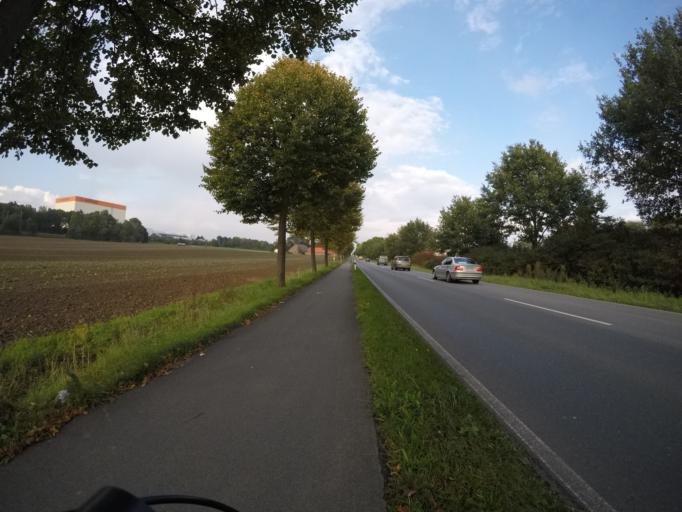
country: DE
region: North Rhine-Westphalia
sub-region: Regierungsbezirk Detmold
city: Herford
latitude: 52.0954
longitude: 8.6320
